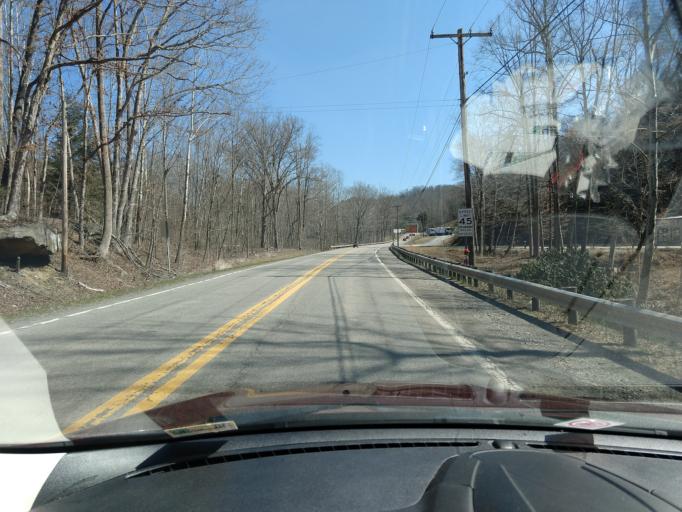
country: US
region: West Virginia
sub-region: Braxton County
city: Sutton
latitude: 38.6889
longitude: -80.6805
